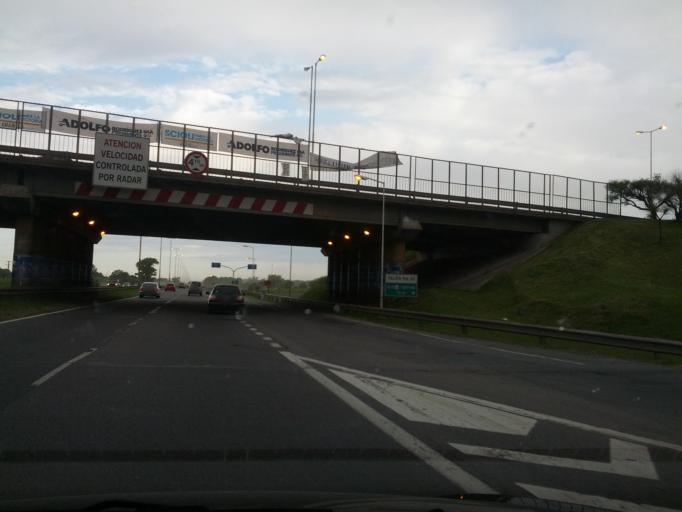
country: AR
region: Buenos Aires
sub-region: Partido de Lujan
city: Lujan
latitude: -34.5737
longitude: -59.0375
